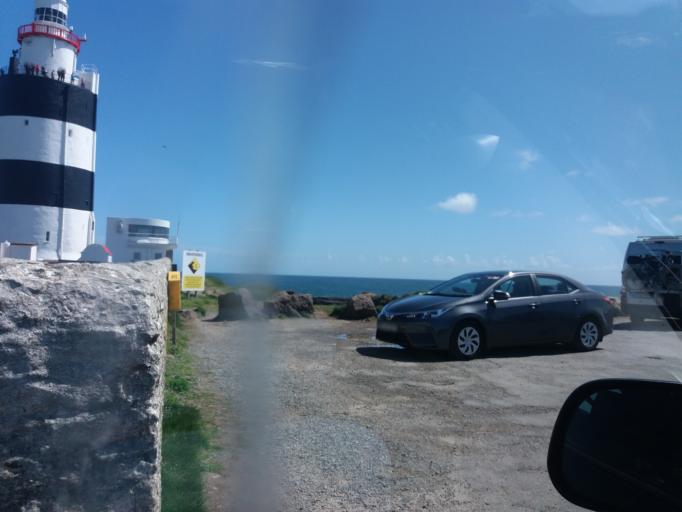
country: IE
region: Munster
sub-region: Waterford
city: Dunmore East
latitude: 52.1240
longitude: -6.9305
